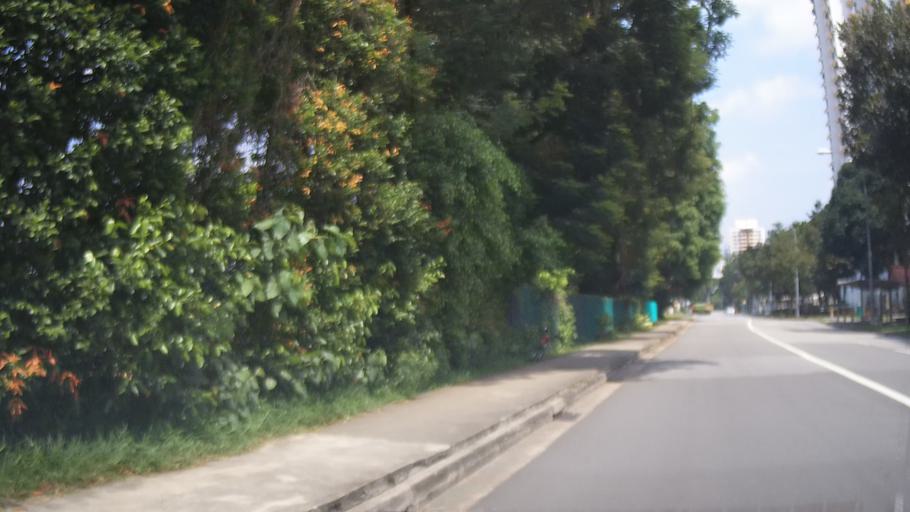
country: SG
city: Singapore
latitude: 1.3187
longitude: 103.8600
